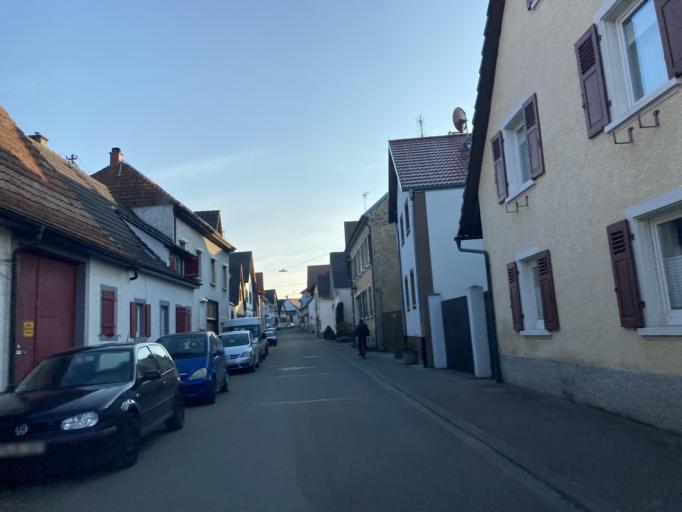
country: DE
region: Baden-Wuerttemberg
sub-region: Freiburg Region
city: Wyhl
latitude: 48.1353
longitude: 7.6563
